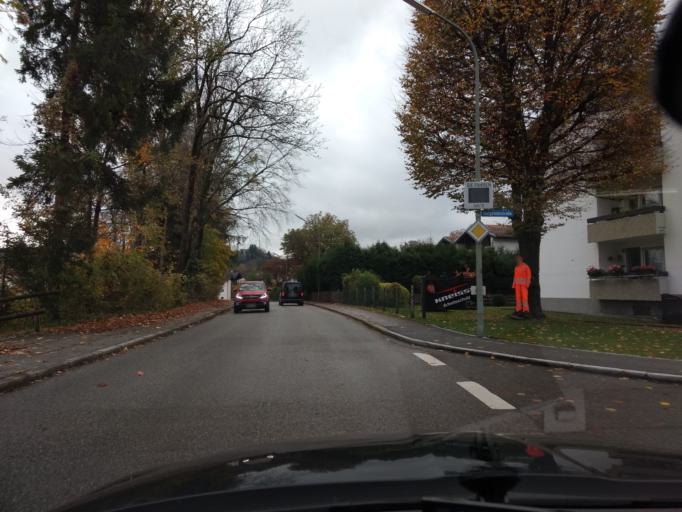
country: DE
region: Bavaria
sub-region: Upper Bavaria
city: Bad Toelz
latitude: 47.7659
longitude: 11.5392
